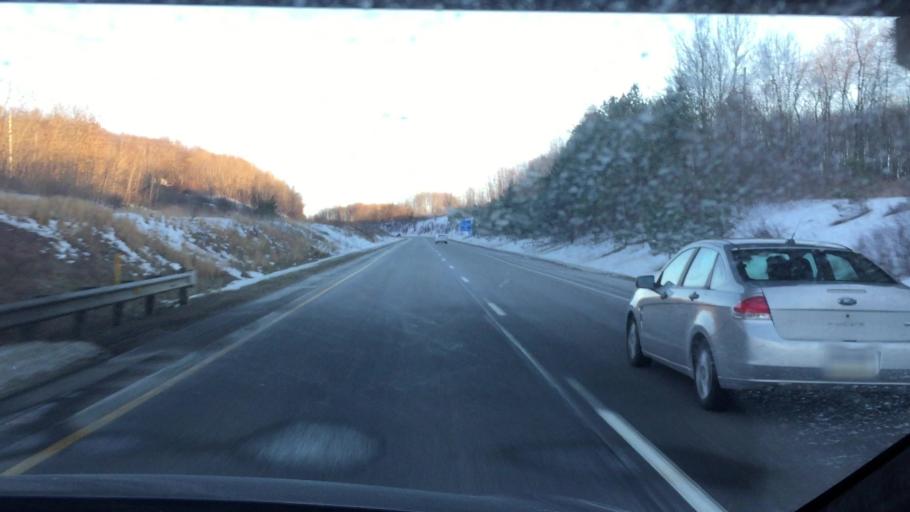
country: US
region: Pennsylvania
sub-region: Crawford County
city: Meadville
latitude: 41.6475
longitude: -80.2039
